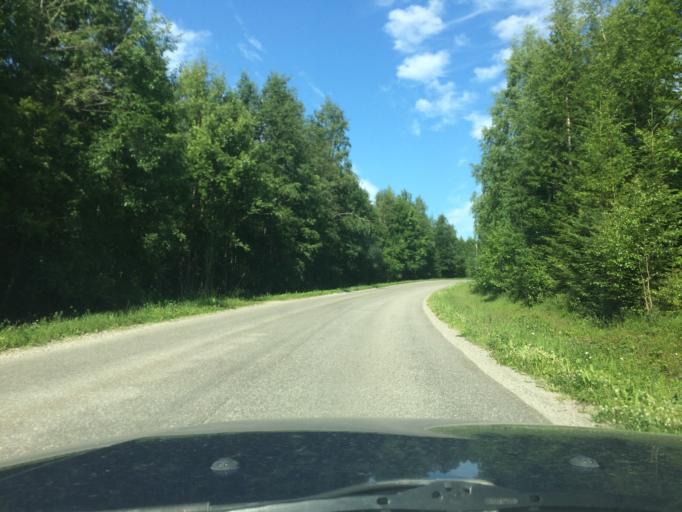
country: SE
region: Norrbotten
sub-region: Pitea Kommun
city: Norrfjarden
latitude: 65.3734
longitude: 21.3913
